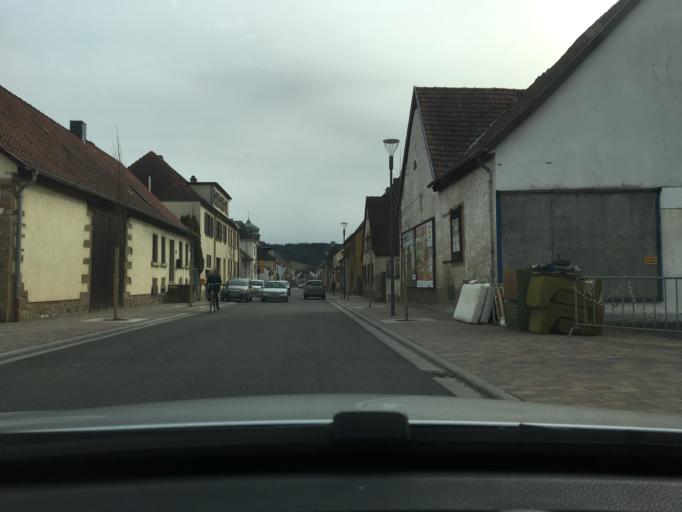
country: DE
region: Rheinland-Pfalz
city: Rockenhausen
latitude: 49.6332
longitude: 7.8240
